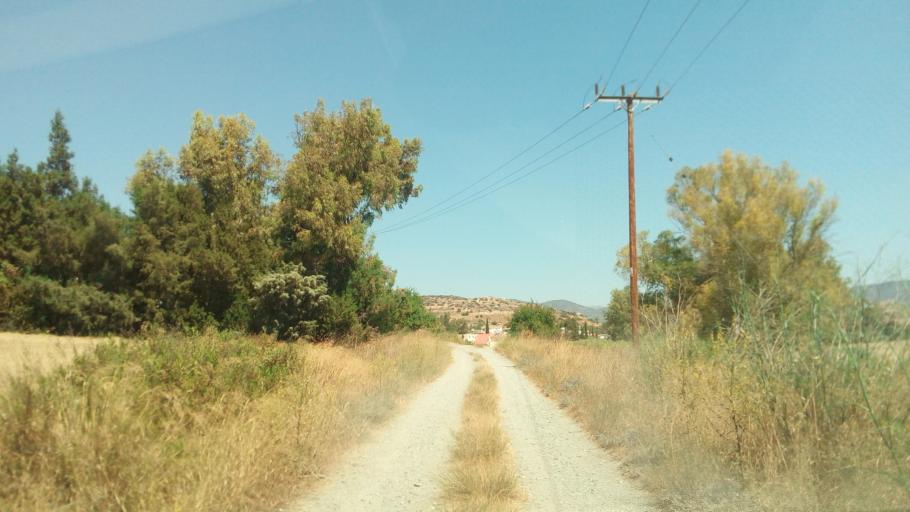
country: CY
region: Limassol
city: Pyrgos
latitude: 34.7345
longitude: 33.1806
